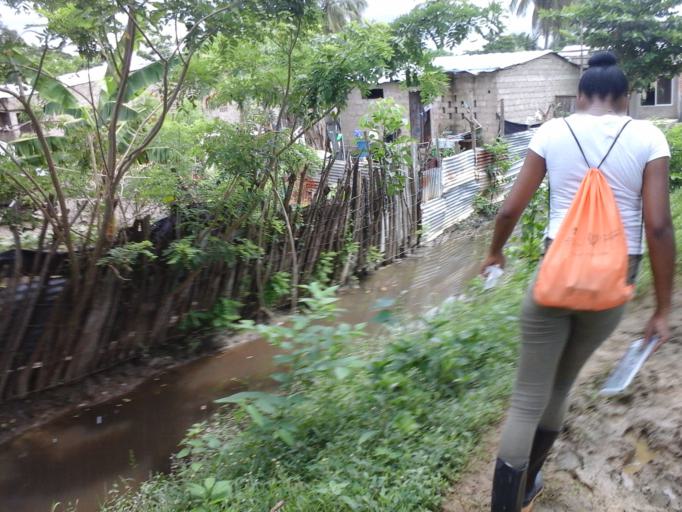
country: CO
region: Bolivar
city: San Pablo
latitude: 10.1465
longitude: -75.2764
